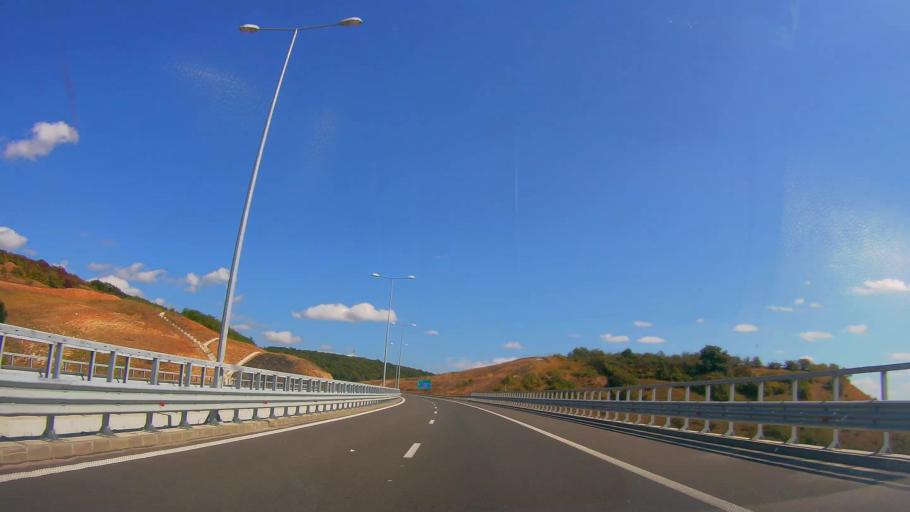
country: RO
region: Cluj
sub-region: Comuna Floresti
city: Luna de Sus
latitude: 46.7774
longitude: 23.4071
